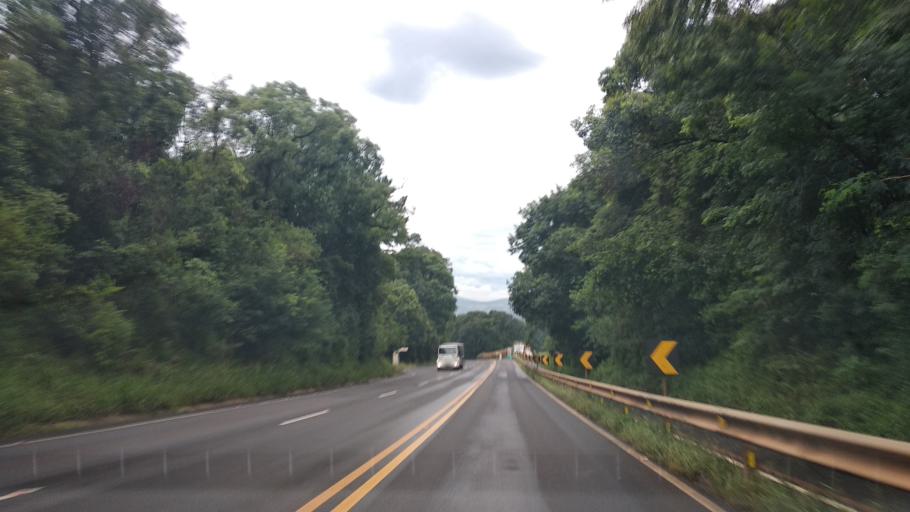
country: BR
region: Santa Catarina
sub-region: Videira
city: Videira
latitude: -27.0829
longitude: -51.2386
